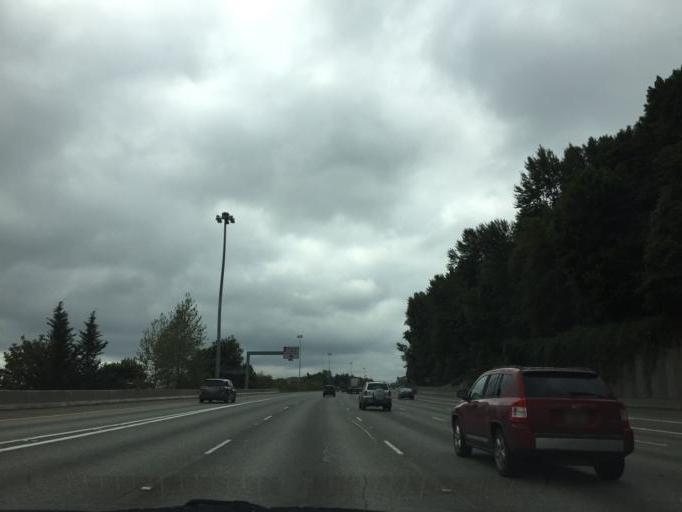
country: US
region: Washington
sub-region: King County
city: Tukwila
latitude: 47.4557
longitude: -122.2642
